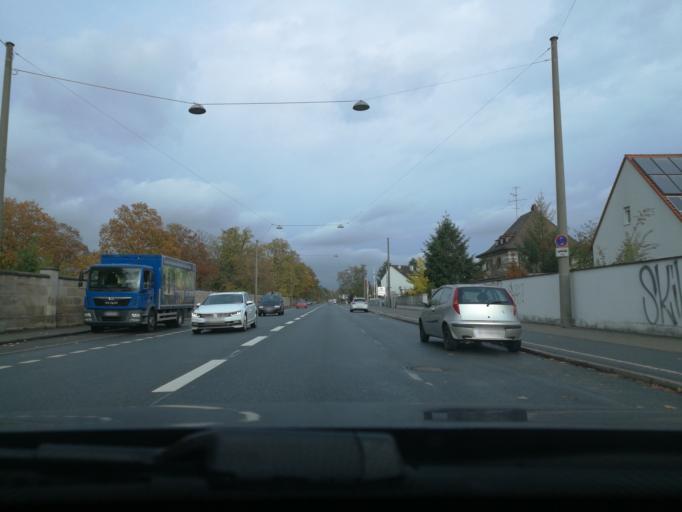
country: DE
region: Bavaria
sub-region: Regierungsbezirk Mittelfranken
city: Furth
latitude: 49.4868
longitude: 10.9956
